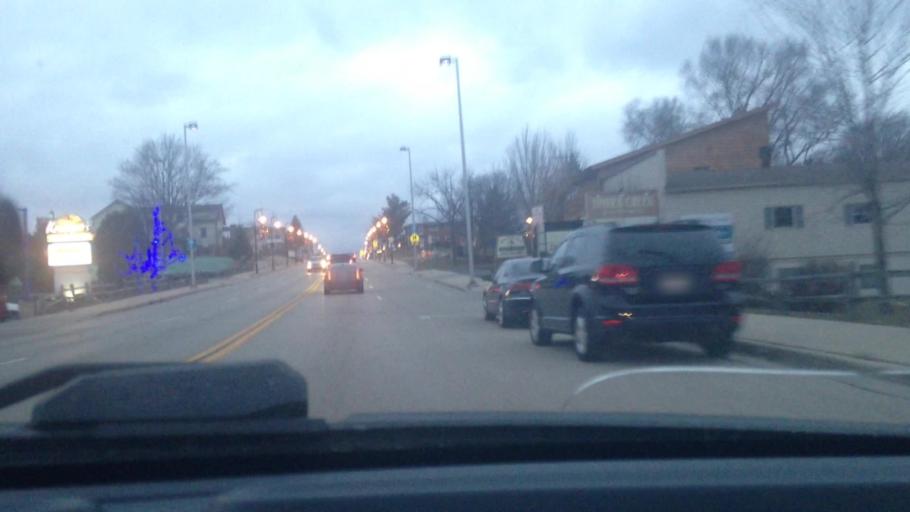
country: US
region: Wisconsin
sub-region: Waukesha County
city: Menomonee Falls
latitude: 43.1758
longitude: -88.1140
